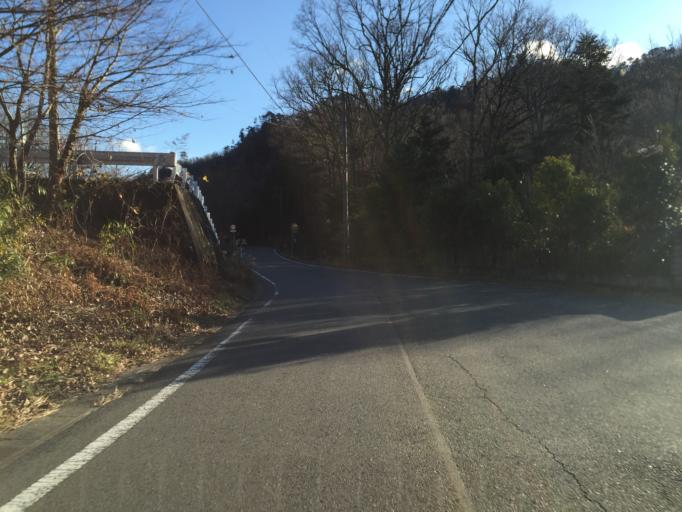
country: JP
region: Fukushima
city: Iwaki
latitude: 37.1861
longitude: 140.8161
